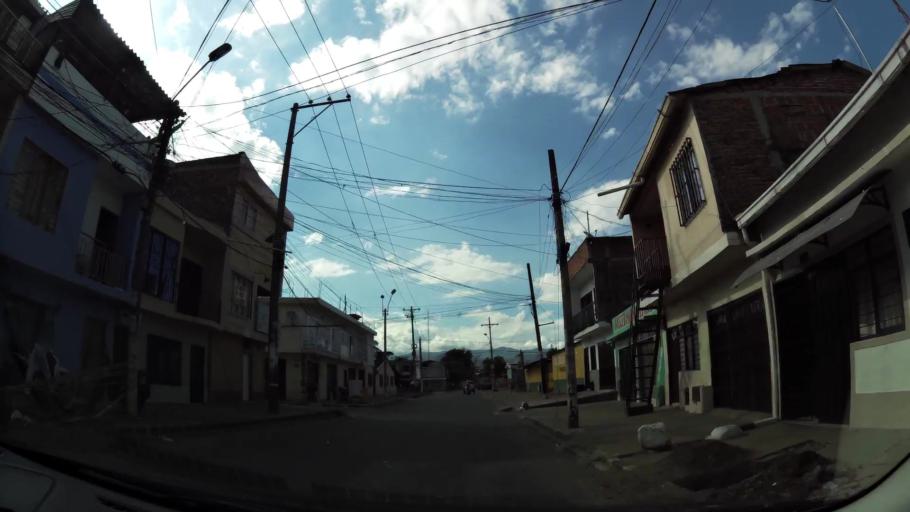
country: CO
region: Valle del Cauca
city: Cali
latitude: 3.4217
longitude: -76.4974
